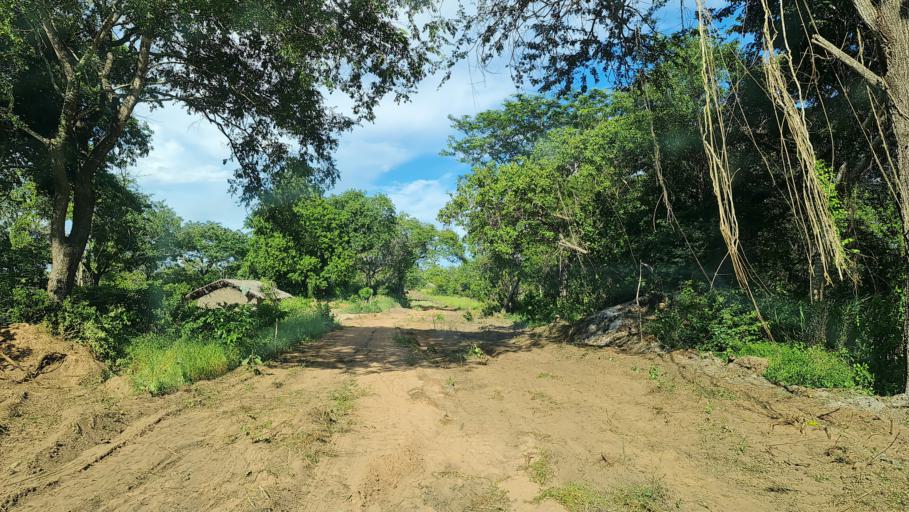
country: MZ
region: Nampula
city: Ilha de Mocambique
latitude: -15.5066
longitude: 40.1469
